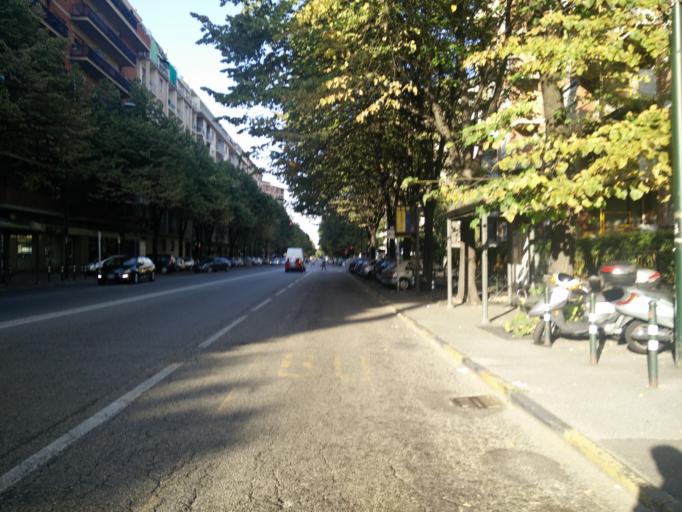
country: IT
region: Piedmont
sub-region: Provincia di Torino
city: Lesna
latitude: 45.0405
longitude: 7.6351
